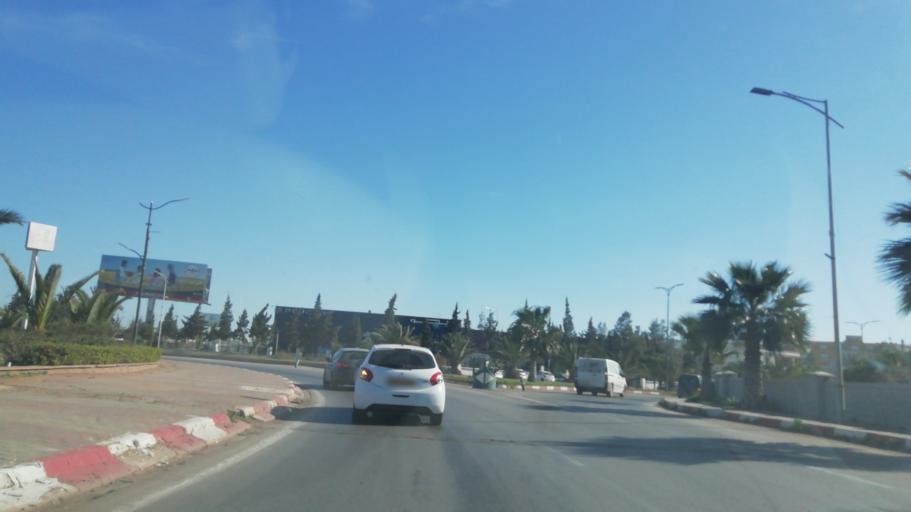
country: DZ
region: Oran
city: Es Senia
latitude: 35.6221
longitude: -0.5925
